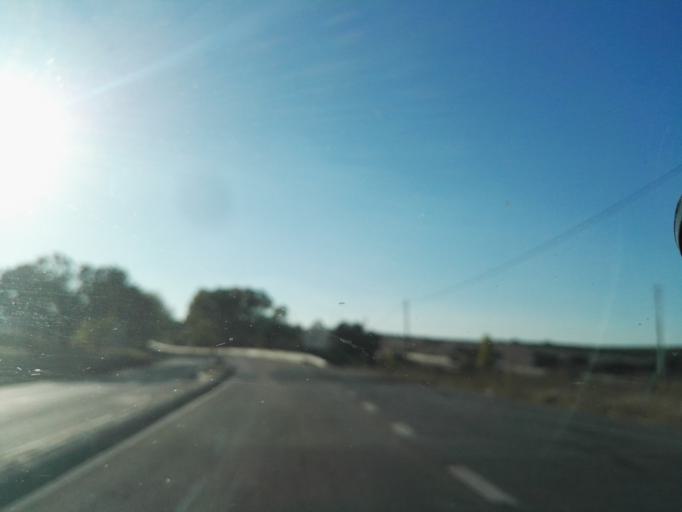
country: PT
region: Evora
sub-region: Vila Vicosa
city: Vila Vicosa
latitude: 38.8541
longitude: -7.3295
